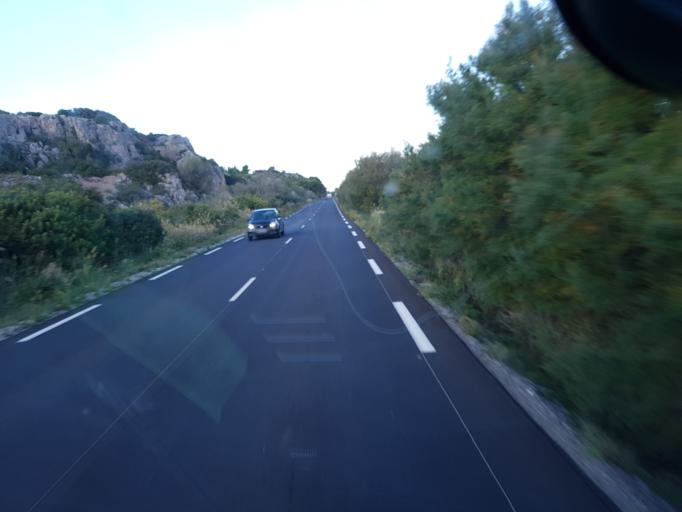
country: FR
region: Languedoc-Roussillon
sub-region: Departement de l'Aude
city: Port-la-Nouvelle
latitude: 42.9909
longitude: 3.0372
